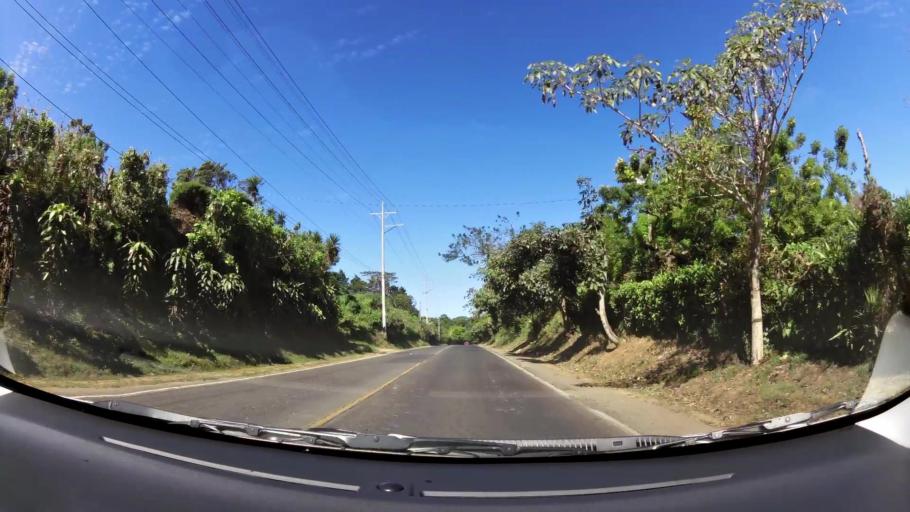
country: SV
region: Ahuachapan
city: Concepcion de Ataco
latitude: 13.8480
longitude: -89.8388
